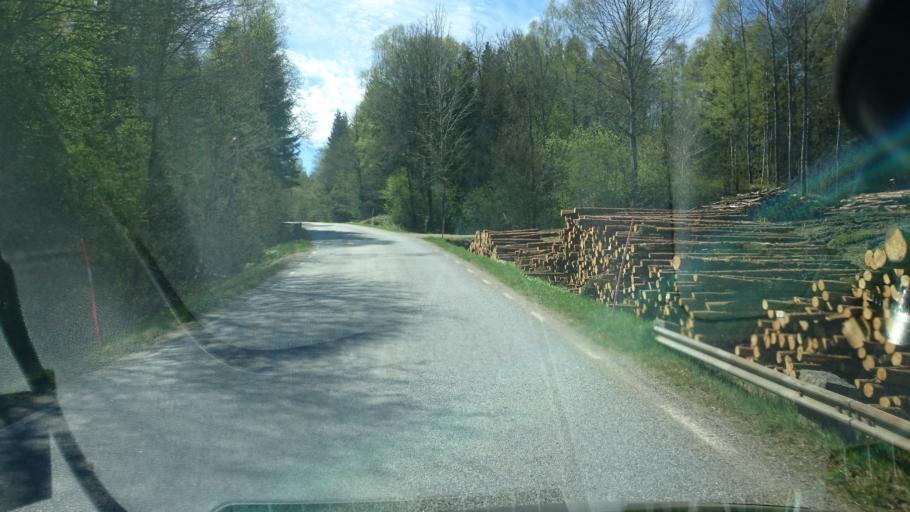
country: SE
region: Vaestra Goetaland
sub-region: Munkedals Kommun
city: Munkedal
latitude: 58.4121
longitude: 11.6740
